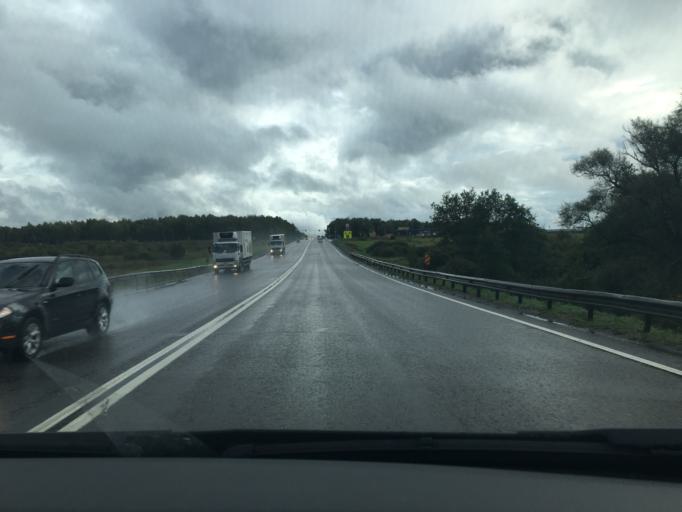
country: RU
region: Kaluga
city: Balabanovo
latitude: 55.1525
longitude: 36.6632
